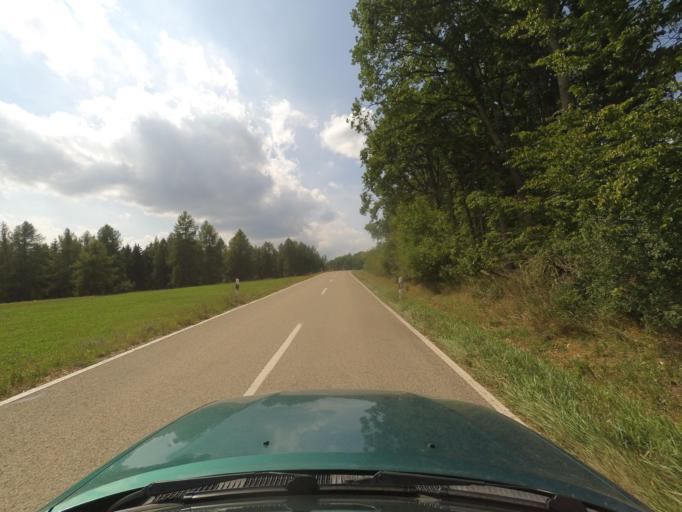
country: DE
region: Bavaria
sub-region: Regierungsbezirk Mittelfranken
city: Raitenbuch
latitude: 49.0169
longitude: 11.1657
